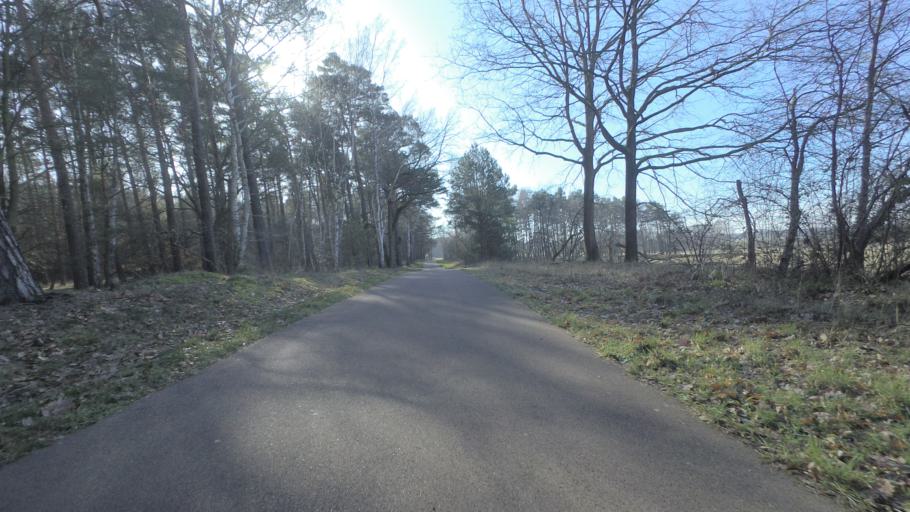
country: DE
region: Brandenburg
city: Juterbog
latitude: 52.0274
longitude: 13.1300
